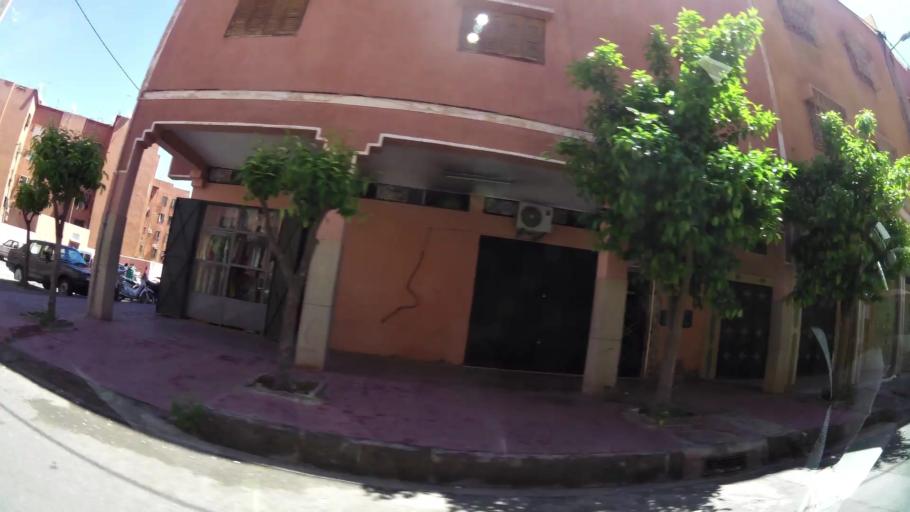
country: MA
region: Marrakech-Tensift-Al Haouz
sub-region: Marrakech
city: Marrakesh
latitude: 31.6330
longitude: -8.0597
